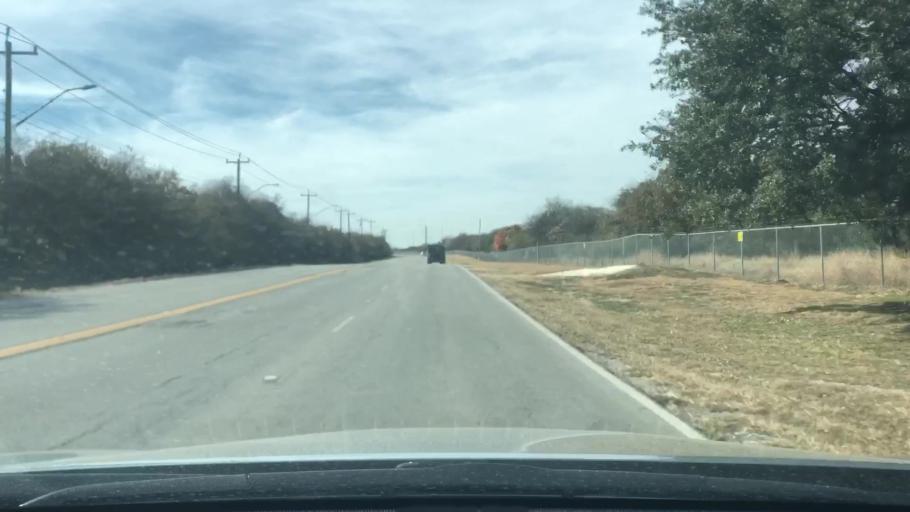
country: US
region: Texas
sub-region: Bexar County
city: Lackland Air Force Base
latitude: 29.4358
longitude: -98.6039
